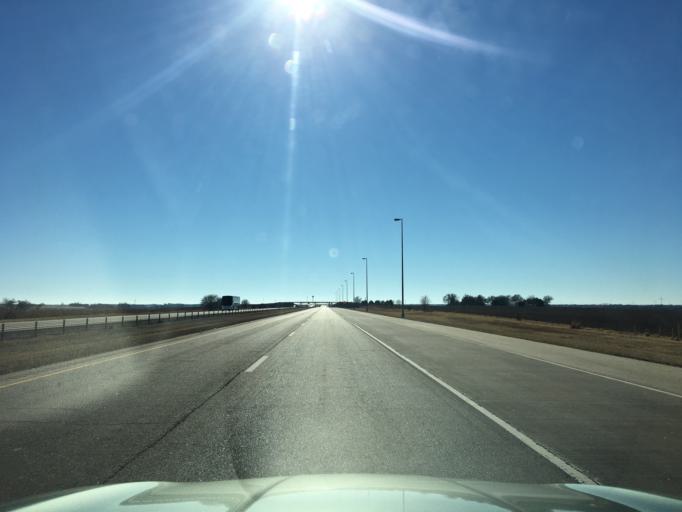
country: US
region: Oklahoma
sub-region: Kay County
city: Blackwell
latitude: 36.9769
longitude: -97.3458
